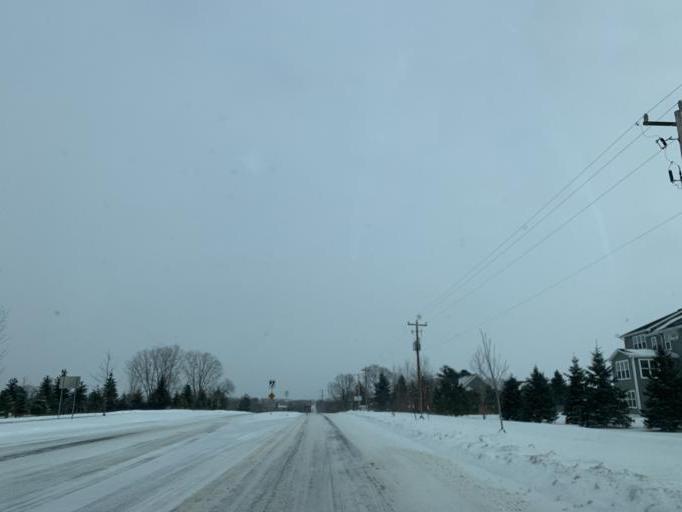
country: US
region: Minnesota
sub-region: Washington County
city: Cottage Grove
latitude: 44.8763
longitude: -92.9182
